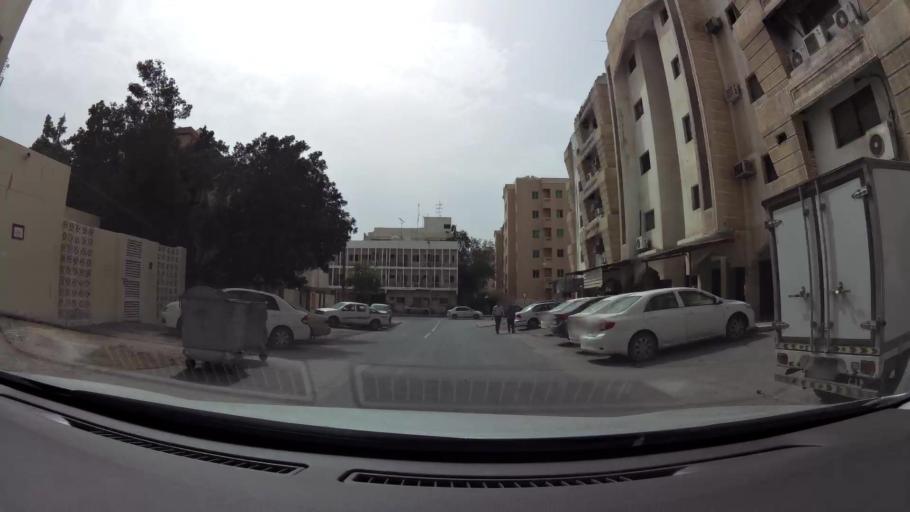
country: QA
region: Baladiyat ad Dawhah
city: Doha
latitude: 25.2665
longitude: 51.5426
